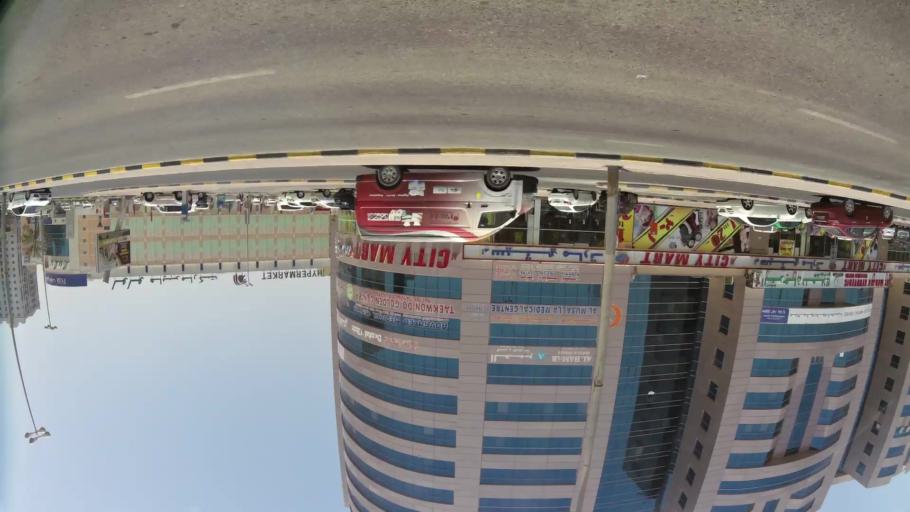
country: AE
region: Ajman
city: Ajman
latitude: 25.4079
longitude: 55.4432
